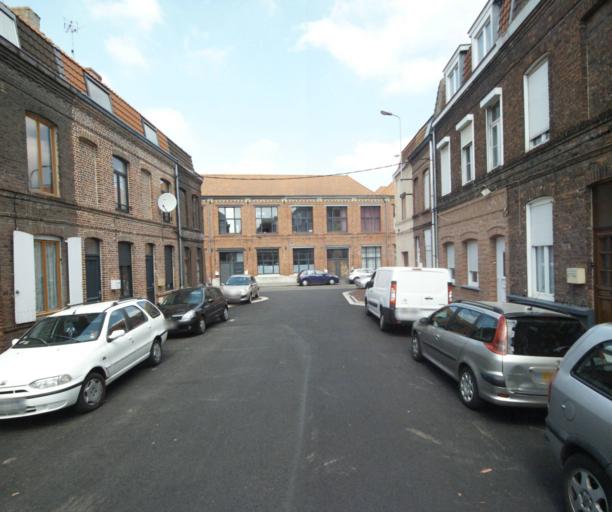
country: FR
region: Nord-Pas-de-Calais
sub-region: Departement du Nord
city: Armentieres
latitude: 50.6910
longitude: 2.8765
